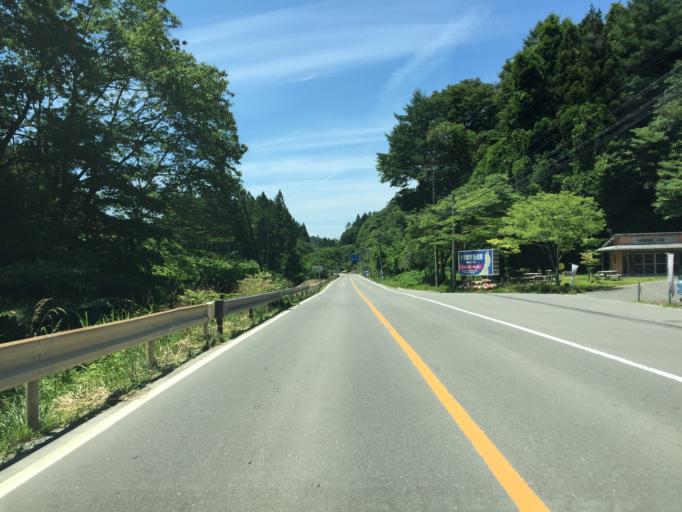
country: JP
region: Fukushima
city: Yanagawamachi-saiwaicho
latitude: 37.7552
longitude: 140.6940
